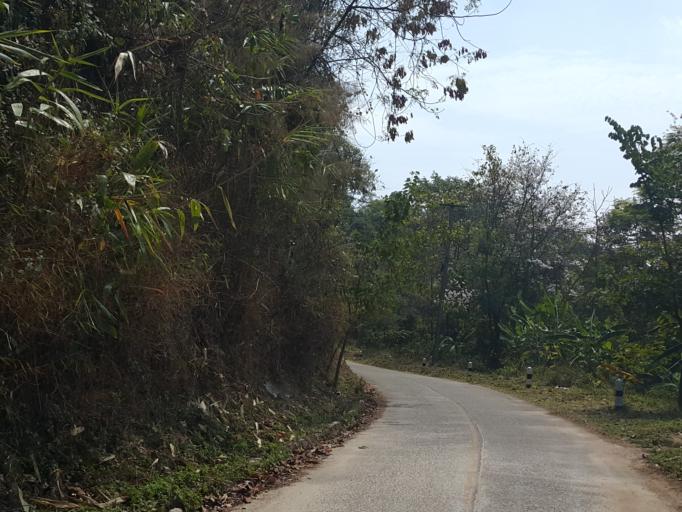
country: TH
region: Lampang
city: Mueang Pan
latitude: 18.8284
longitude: 99.4026
